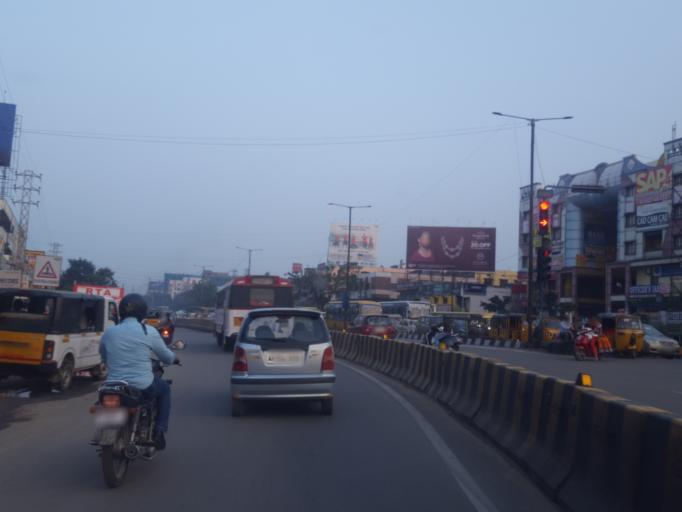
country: IN
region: Telangana
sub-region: Medak
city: Serilingampalle
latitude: 17.4953
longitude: 78.3170
